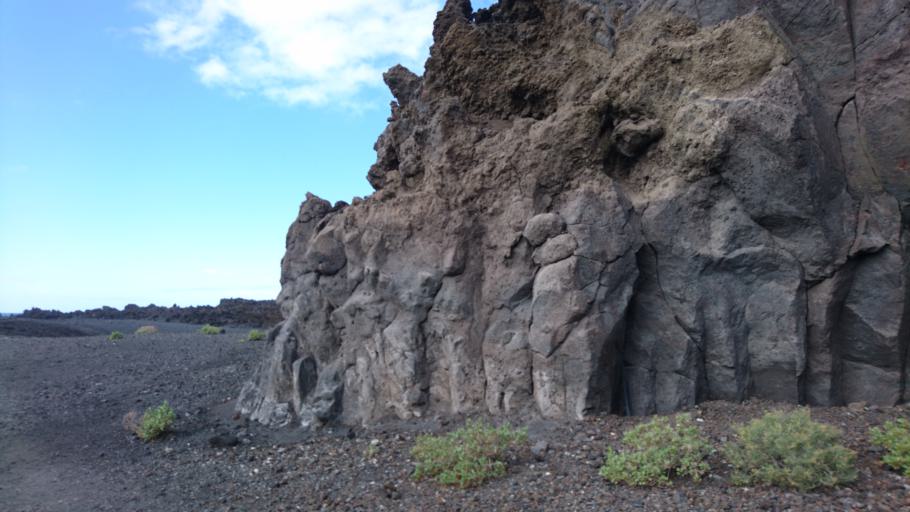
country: ES
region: Canary Islands
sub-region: Provincia de Santa Cruz de Tenerife
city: Fuencaliente de la Palma
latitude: 28.4598
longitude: -17.8509
